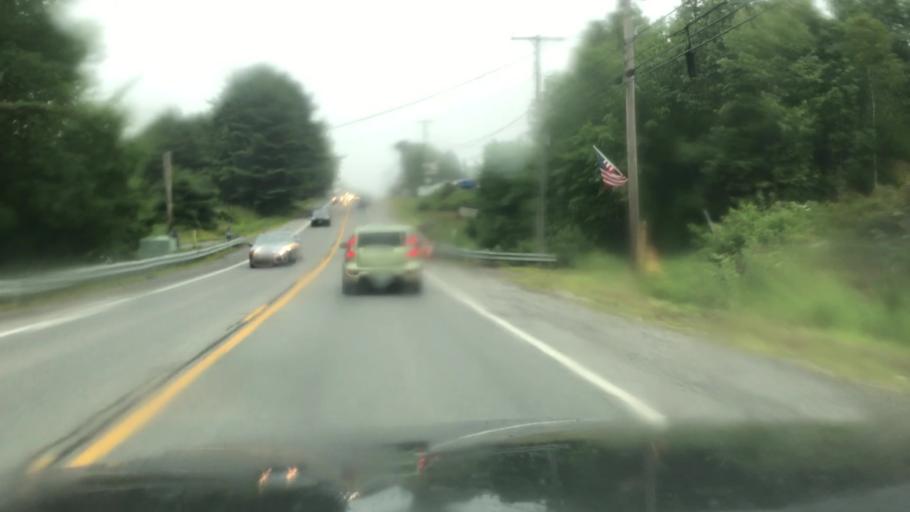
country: US
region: Maine
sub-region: Lincoln County
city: Wiscasset
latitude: 43.9902
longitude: -69.6908
